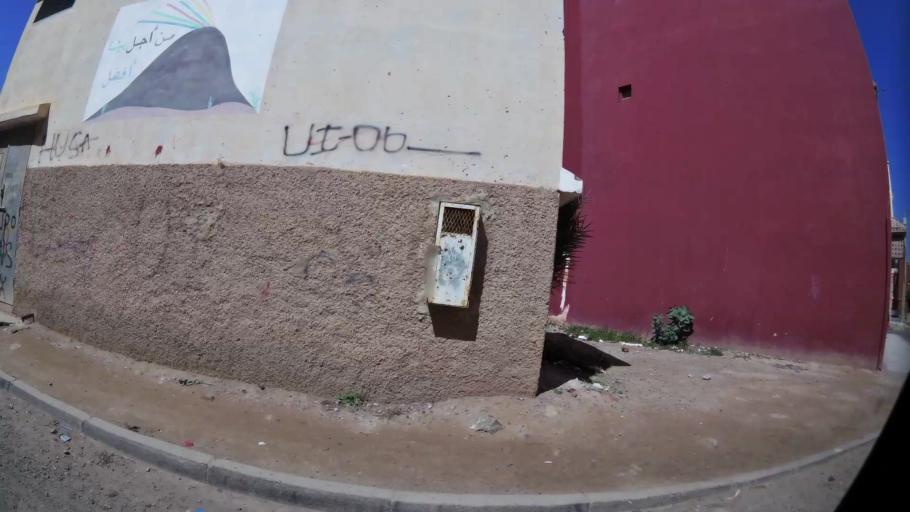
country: MA
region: Souss-Massa-Draa
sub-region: Inezgane-Ait Mellou
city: Inezgane
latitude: 30.3317
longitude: -9.5057
